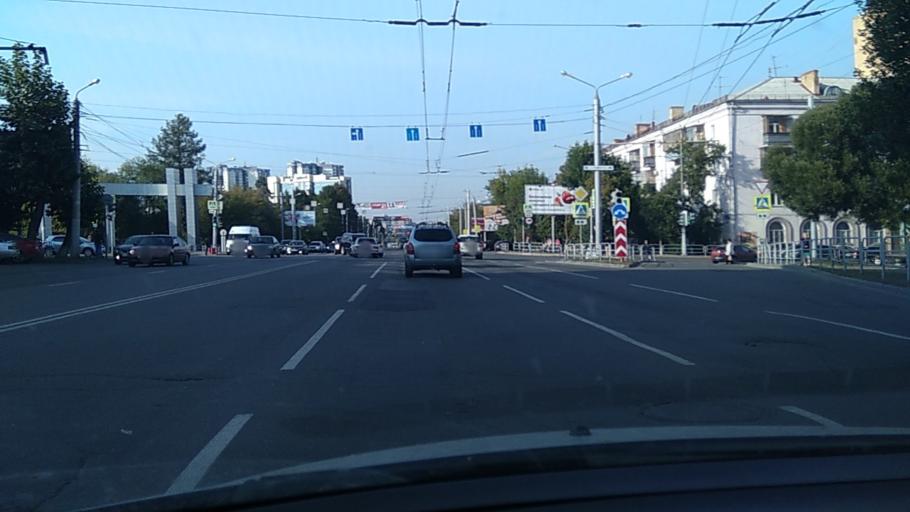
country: RU
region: Chelyabinsk
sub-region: Gorod Chelyabinsk
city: Chelyabinsk
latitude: 55.1617
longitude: 61.3811
